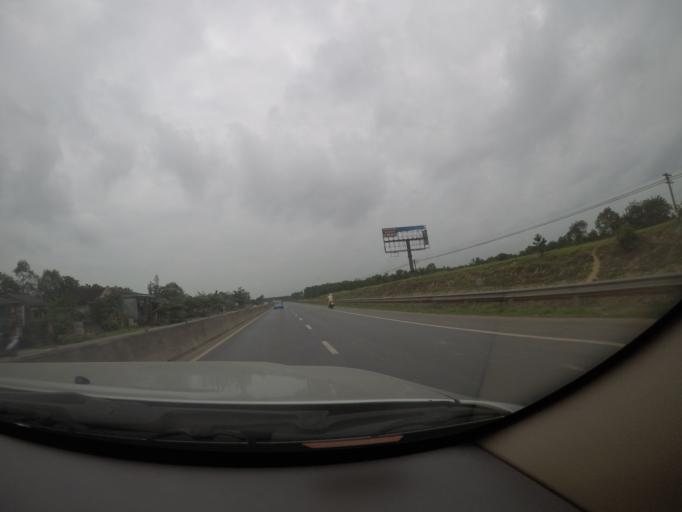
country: VN
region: Quang Tri
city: Hai Lang
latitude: 16.7004
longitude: 107.2275
